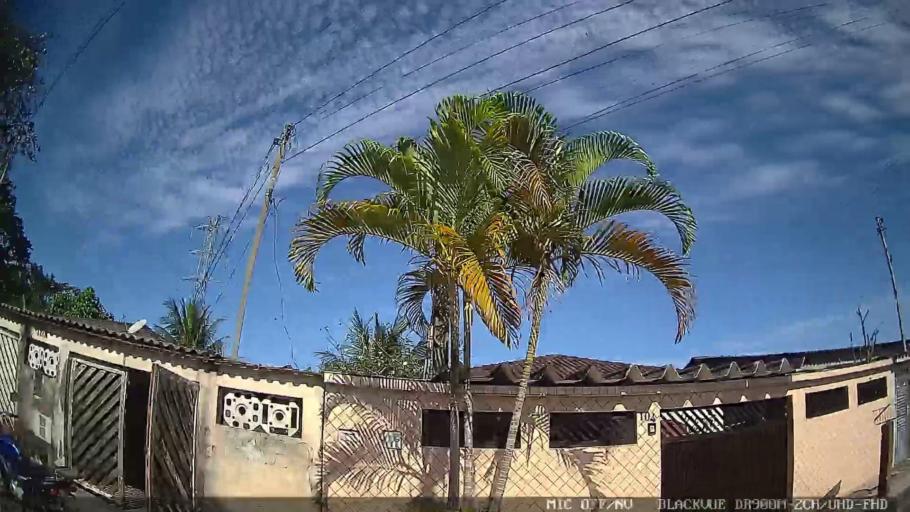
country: BR
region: Sao Paulo
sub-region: Santos
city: Santos
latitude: -23.9464
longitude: -46.2833
